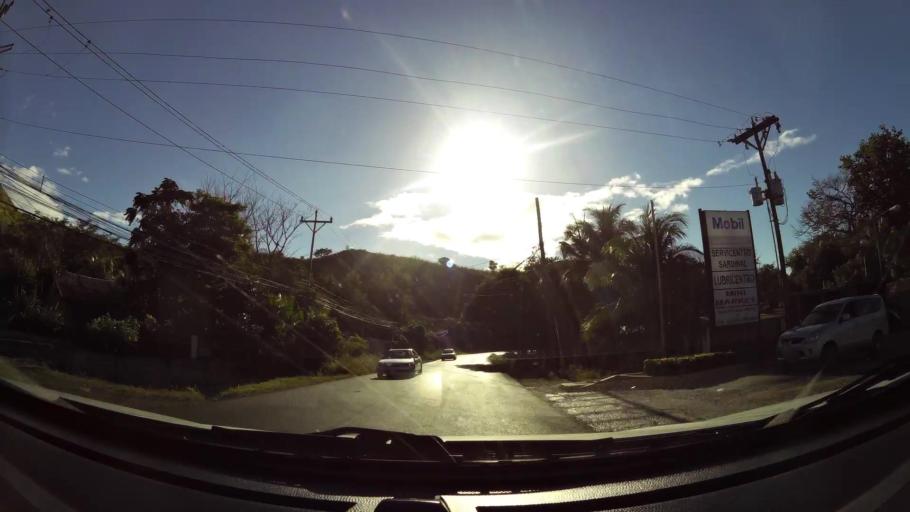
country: CR
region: Guanacaste
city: Sardinal
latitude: 10.5230
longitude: -85.6507
